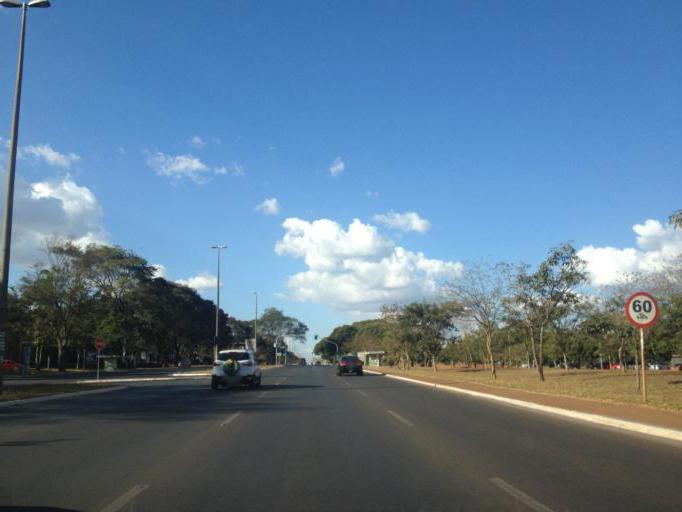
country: BR
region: Federal District
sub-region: Brasilia
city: Brasilia
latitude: -15.8320
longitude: -47.9103
